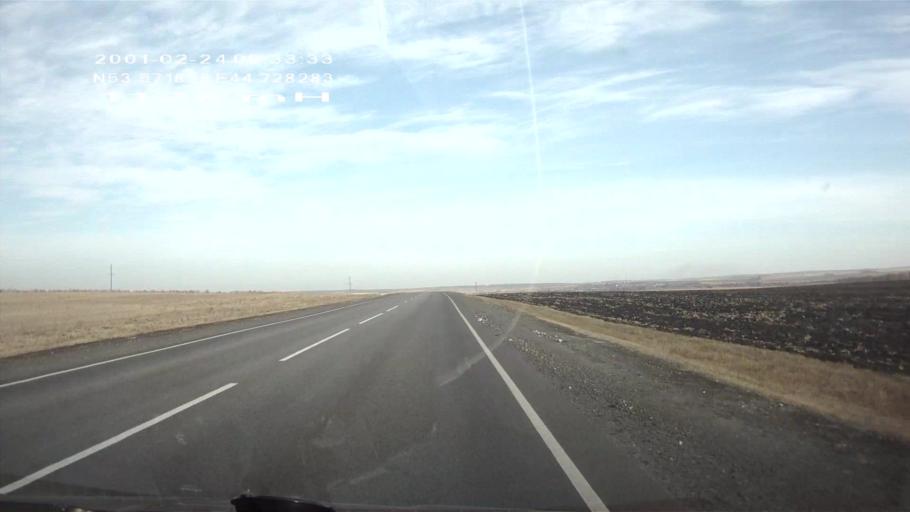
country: RU
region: Penza
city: Mokshan
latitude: 53.5718
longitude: 44.7283
